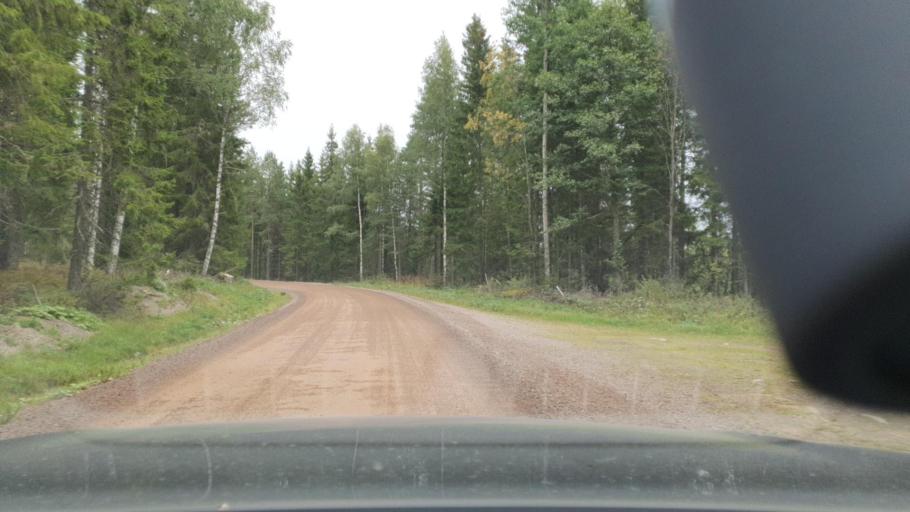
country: SE
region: Vaermland
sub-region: Arvika Kommun
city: Arvika
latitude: 59.9652
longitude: 12.6591
